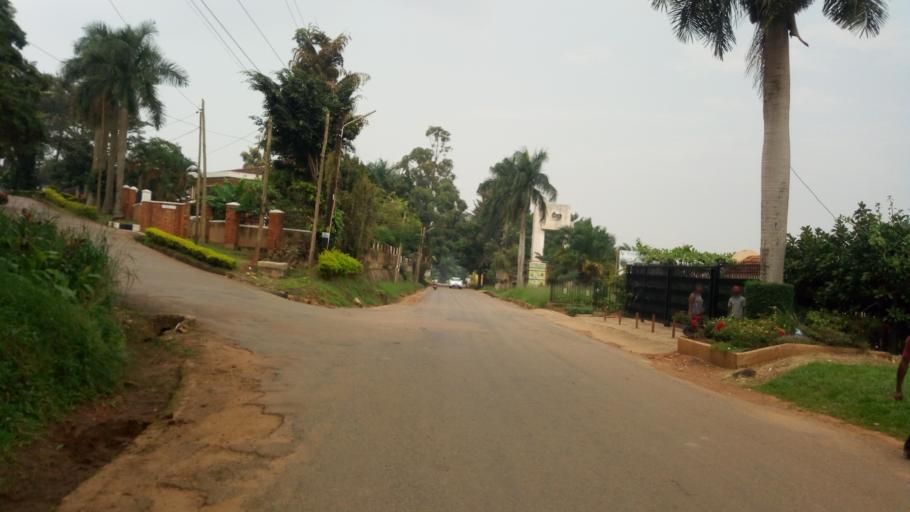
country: UG
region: Central Region
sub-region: Kampala District
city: Kampala
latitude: 0.3081
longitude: 32.6231
